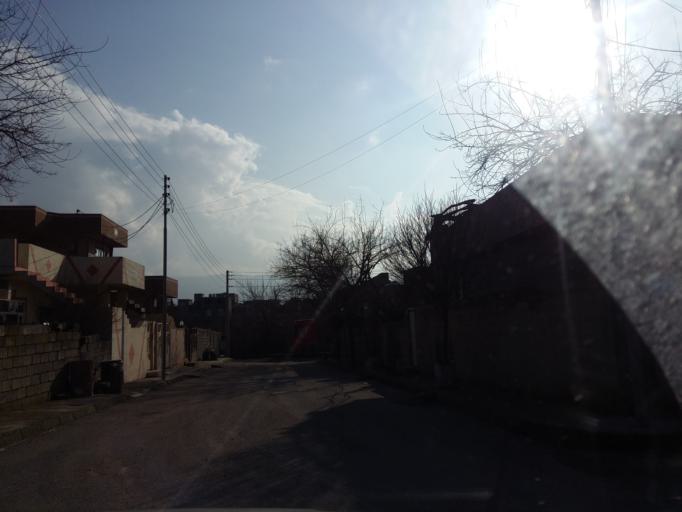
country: IQ
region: As Sulaymaniyah
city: Qeladize
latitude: 36.1761
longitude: 45.1397
